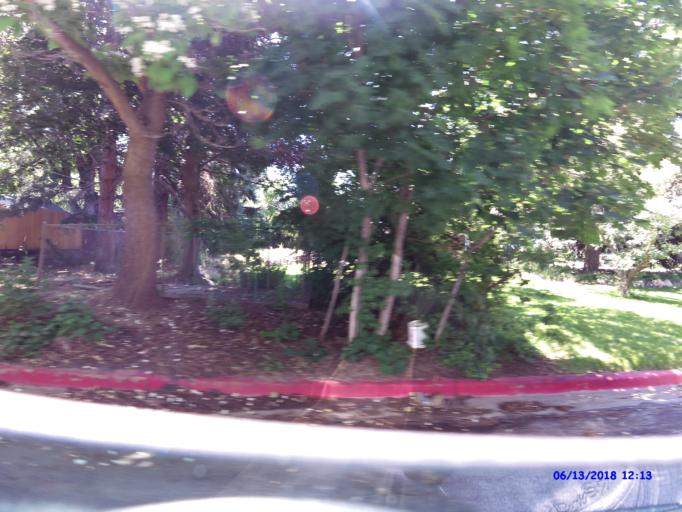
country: US
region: Utah
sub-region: Weber County
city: Ogden
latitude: 41.2148
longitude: -111.9343
